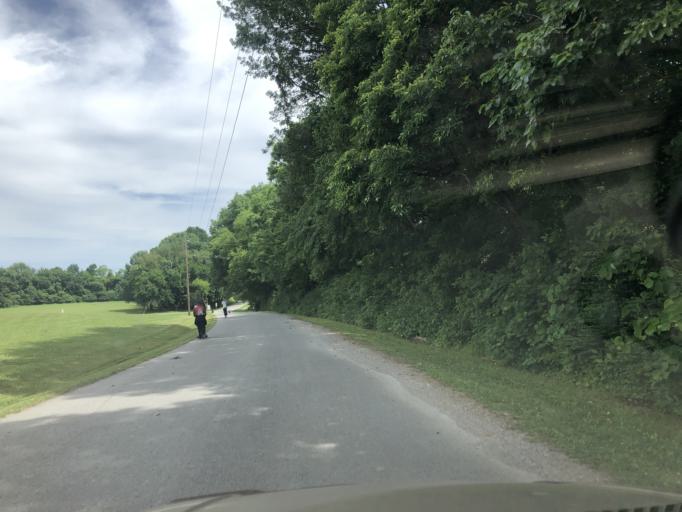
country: US
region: Tennessee
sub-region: Davidson County
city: Lakewood
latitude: 36.2516
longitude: -86.6036
